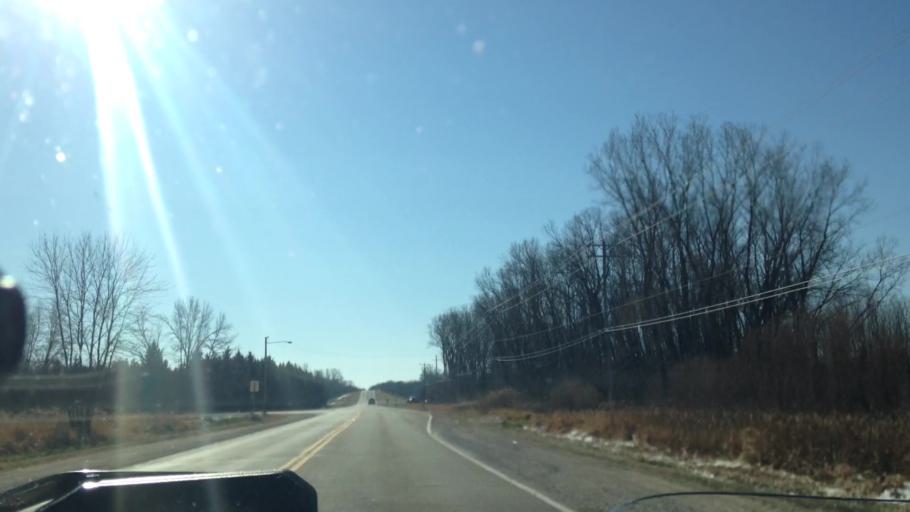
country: US
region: Wisconsin
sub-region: Washington County
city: Germantown
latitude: 43.2151
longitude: -88.1425
